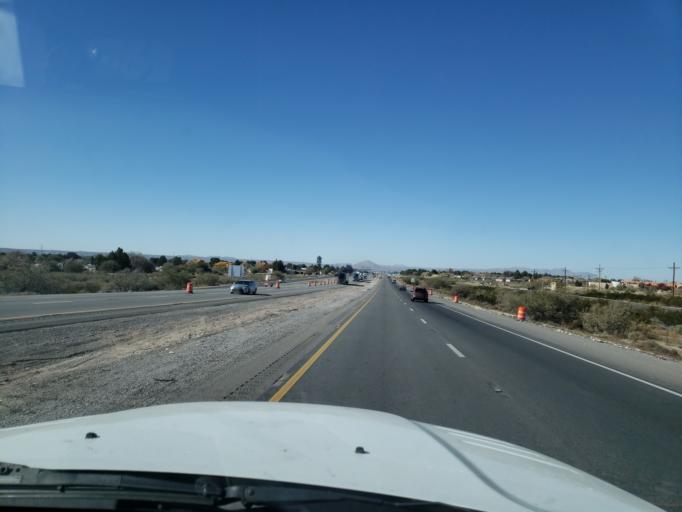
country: US
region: New Mexico
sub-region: Dona Ana County
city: University Park
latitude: 32.2664
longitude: -106.7402
